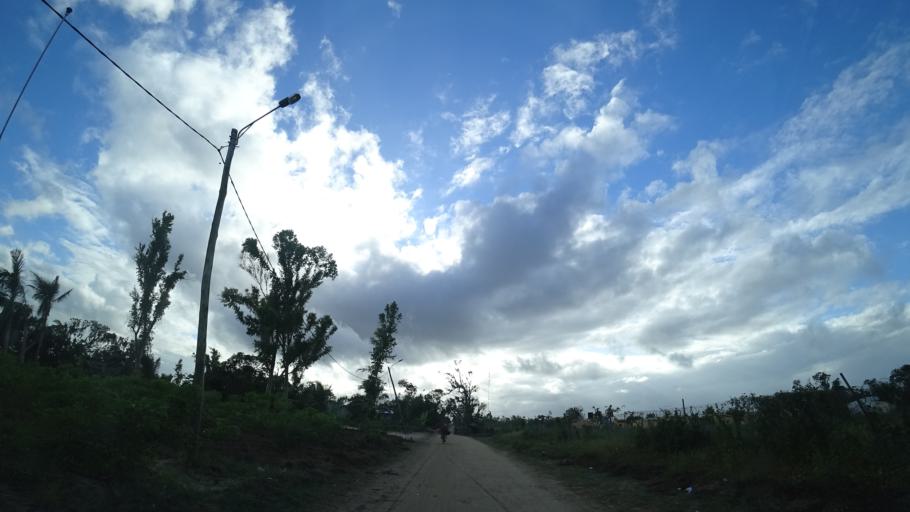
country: MZ
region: Sofala
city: Beira
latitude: -19.7156
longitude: 35.0083
